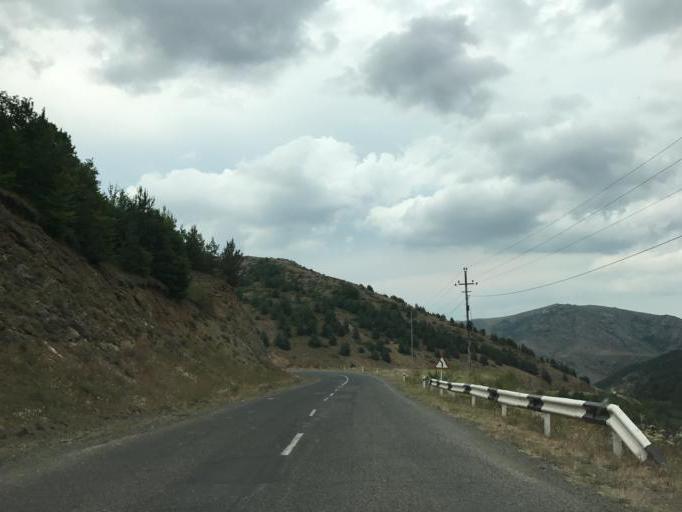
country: AZ
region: Susa
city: Shushi
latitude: 39.7012
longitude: 46.6520
